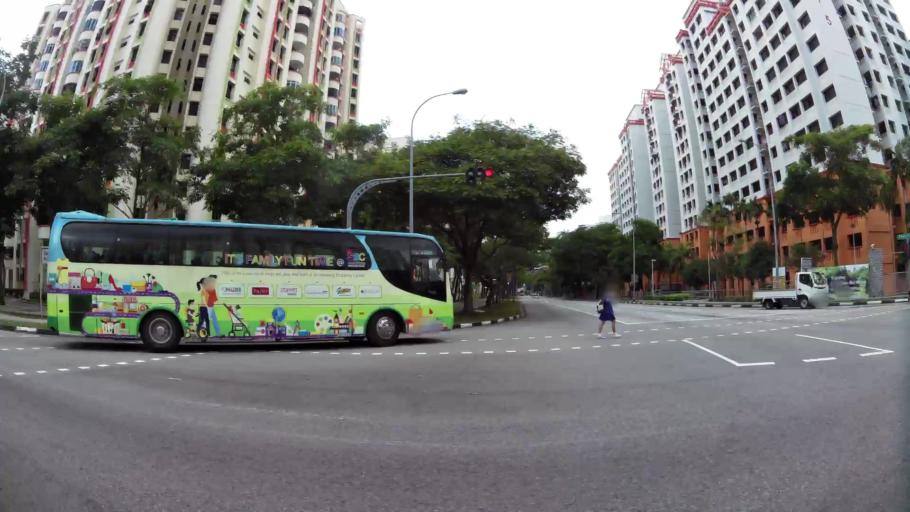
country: MY
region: Johor
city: Johor Bahru
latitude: 1.4508
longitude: 103.8176
